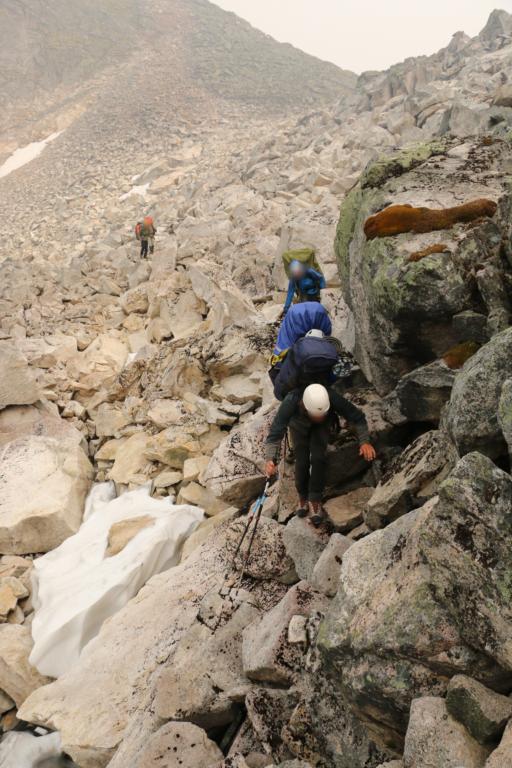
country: RU
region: Respublika Buryatiya
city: Kichera
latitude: 56.2304
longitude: 110.8650
